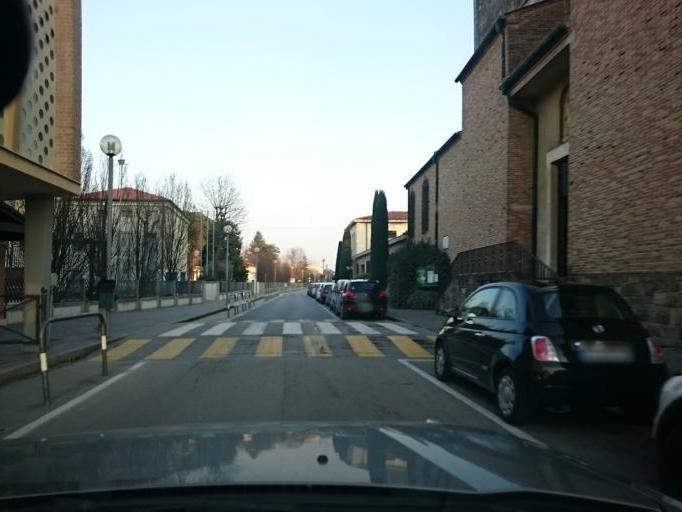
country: IT
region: Veneto
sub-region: Provincia di Padova
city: Abano Terme
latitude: 45.3607
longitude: 11.7905
